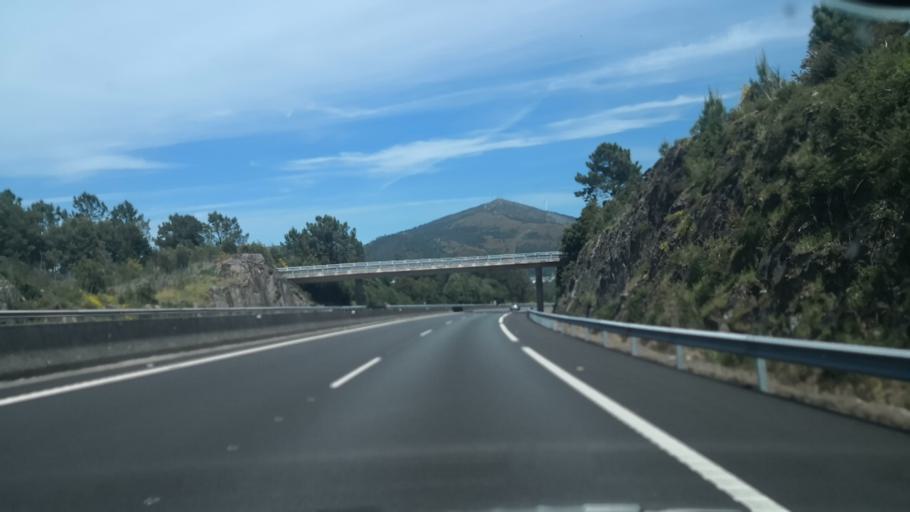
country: ES
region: Galicia
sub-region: Provincia de Pontevedra
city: Valga
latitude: 42.7222
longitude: -8.6407
